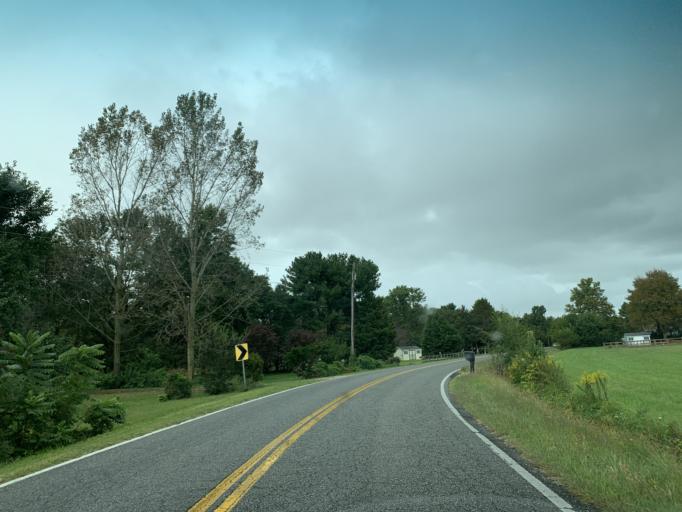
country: US
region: Maryland
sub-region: Caroline County
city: Denton
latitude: 38.9079
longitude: -75.8527
